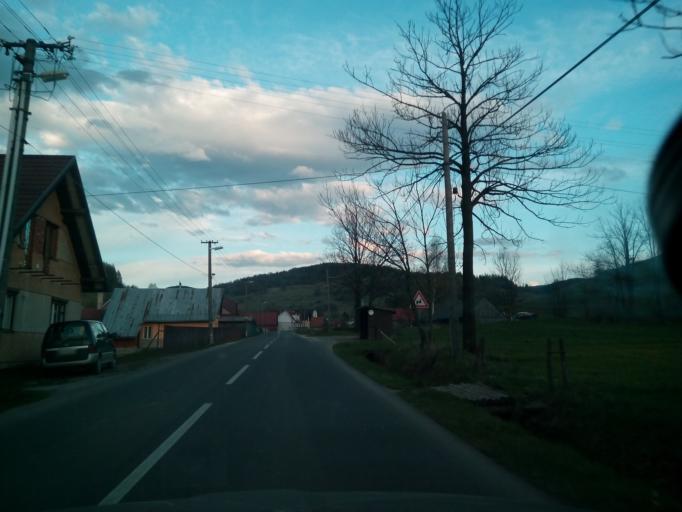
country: SK
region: Presovsky
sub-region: Okres Poprad
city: Zdiar
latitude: 49.3018
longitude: 20.3760
